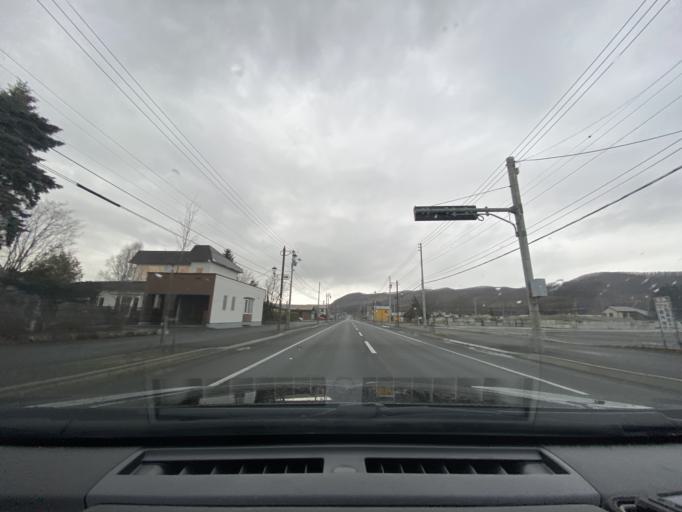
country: JP
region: Hokkaido
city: Otofuke
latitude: 43.2486
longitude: 143.5473
